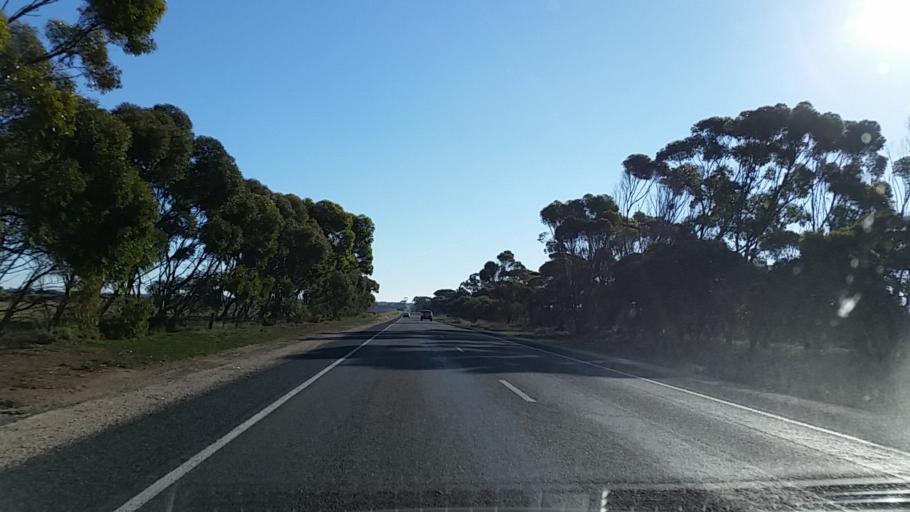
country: AU
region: South Australia
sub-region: Mount Barker
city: Callington
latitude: -35.1171
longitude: 139.1212
